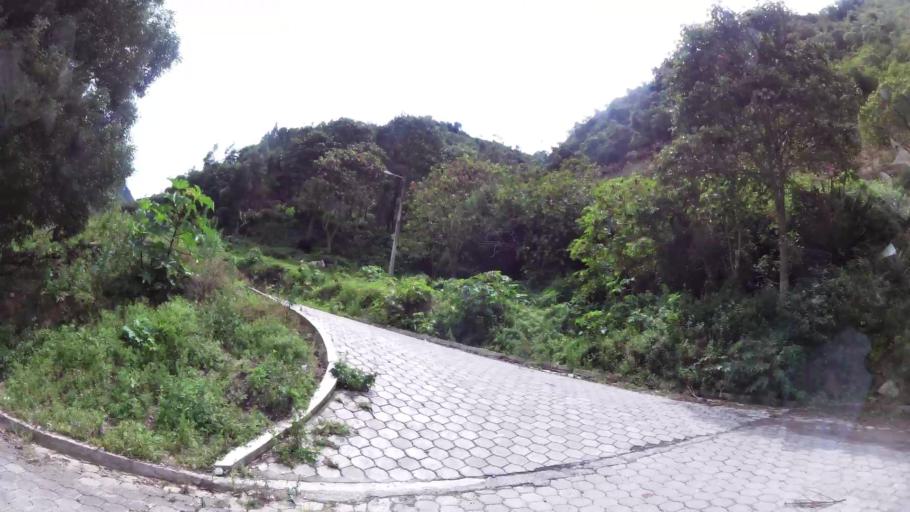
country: EC
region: Tungurahua
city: Banos
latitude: -1.3972
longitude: -78.3931
